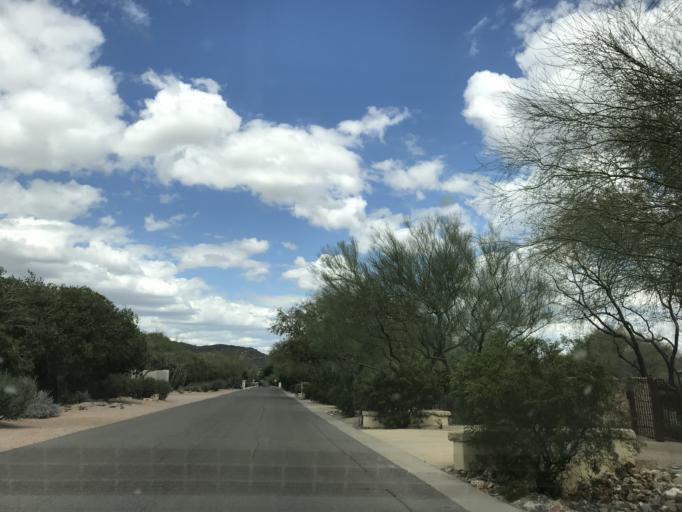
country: US
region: Arizona
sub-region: Maricopa County
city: Paradise Valley
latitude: 33.5192
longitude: -111.9454
